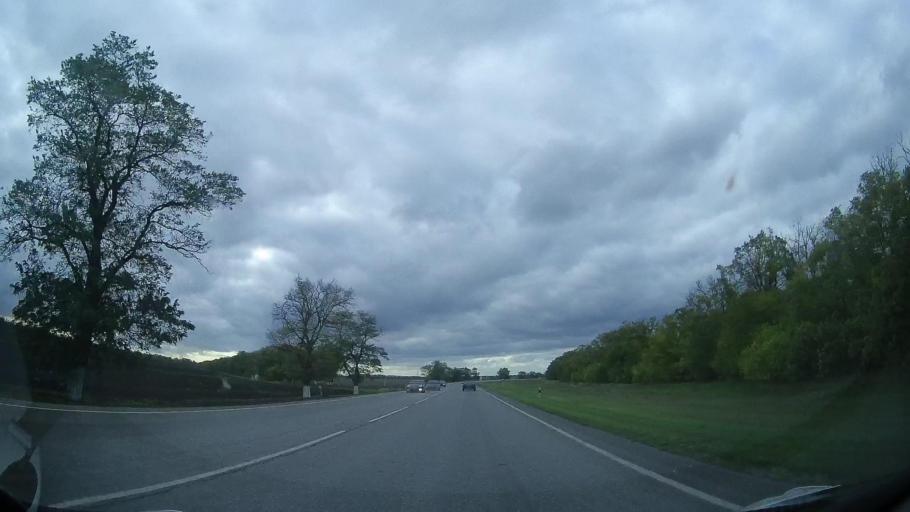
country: RU
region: Rostov
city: Zernograd
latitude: 46.8158
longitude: 40.2708
